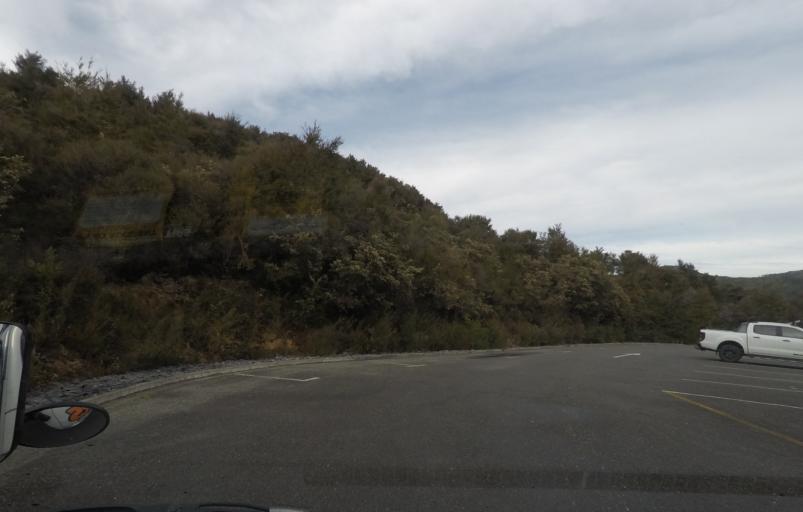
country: NZ
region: Tasman
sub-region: Tasman District
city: Takaka
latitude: -40.8479
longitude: 172.7711
